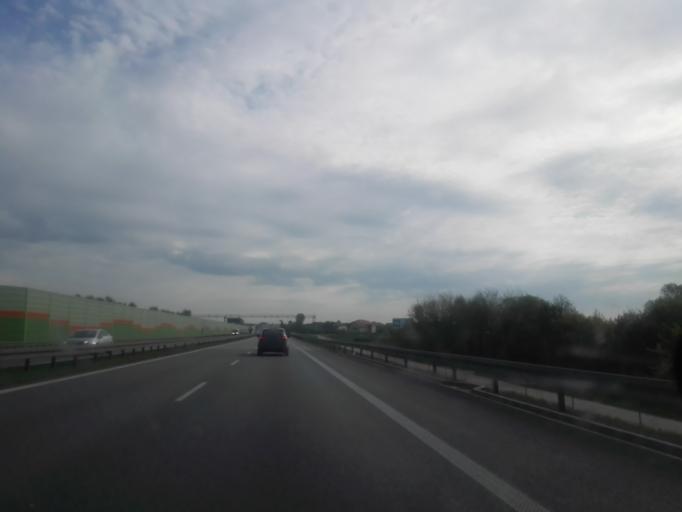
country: PL
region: Lodz Voivodeship
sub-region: Powiat tomaszowski
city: Tomaszow Mazowiecki
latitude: 51.5344
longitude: 19.9551
